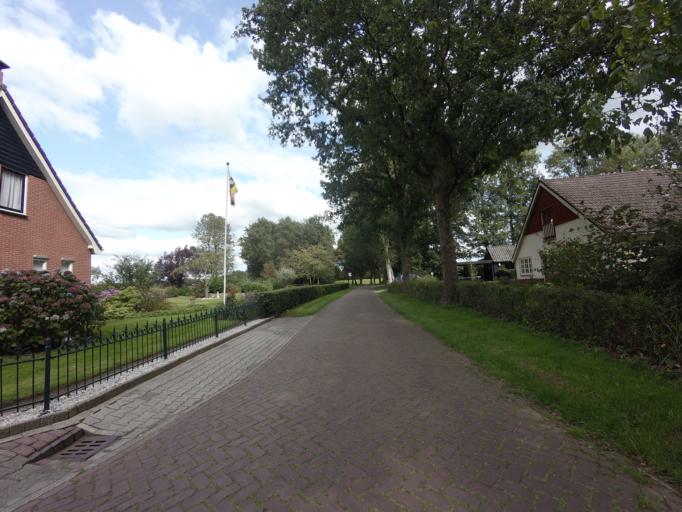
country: NL
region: Drenthe
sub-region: Gemeente De Wolden
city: Ruinen
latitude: 52.7658
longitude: 6.3612
